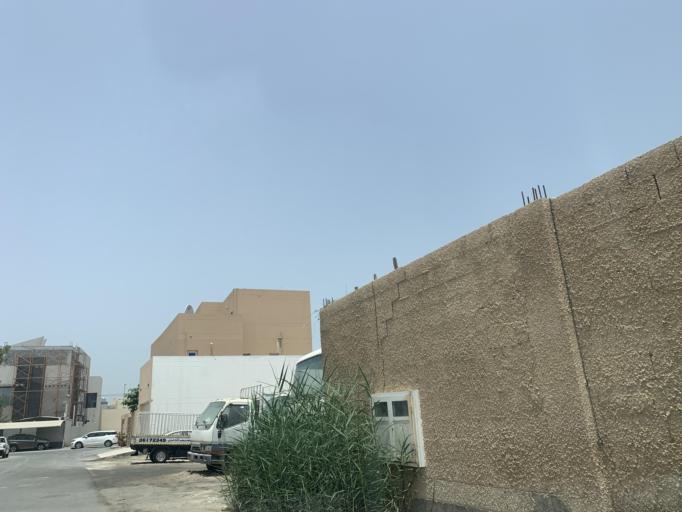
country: BH
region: Northern
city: Sitrah
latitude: 26.1451
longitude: 50.5906
